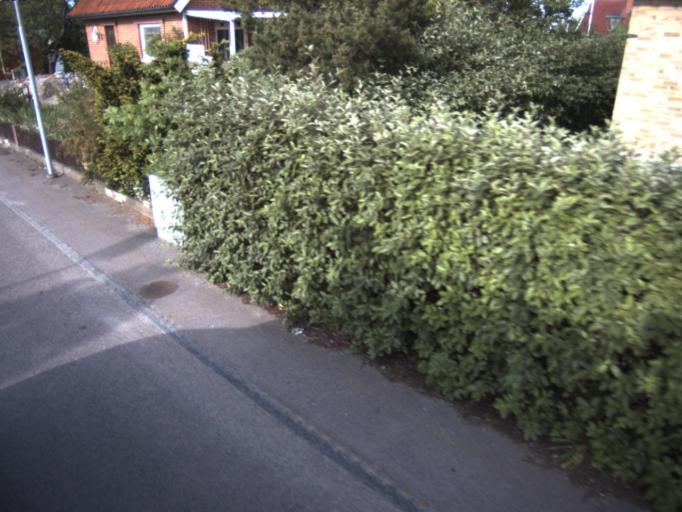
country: SE
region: Skane
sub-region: Helsingborg
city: Odakra
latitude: 56.1063
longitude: 12.7489
